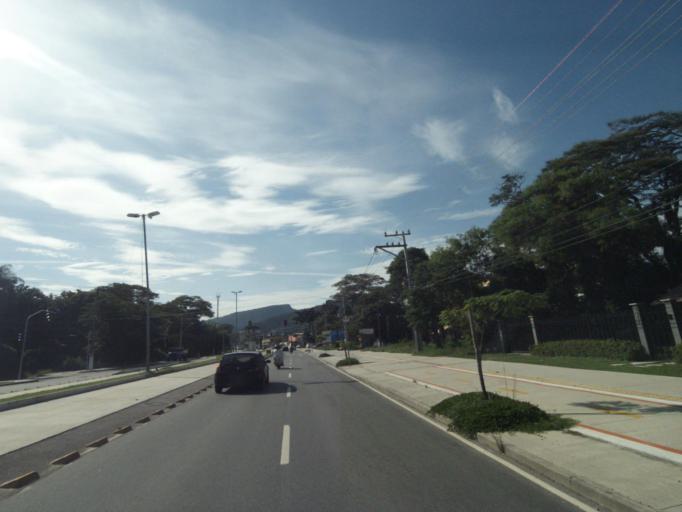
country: BR
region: Rio de Janeiro
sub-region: Niteroi
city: Niteroi
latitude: -22.9501
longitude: -43.0293
